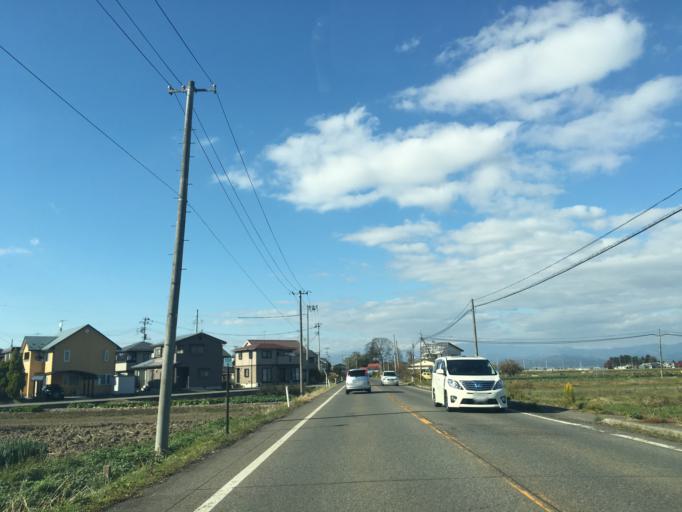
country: JP
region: Fukushima
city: Kitakata
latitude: 37.5489
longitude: 139.8711
